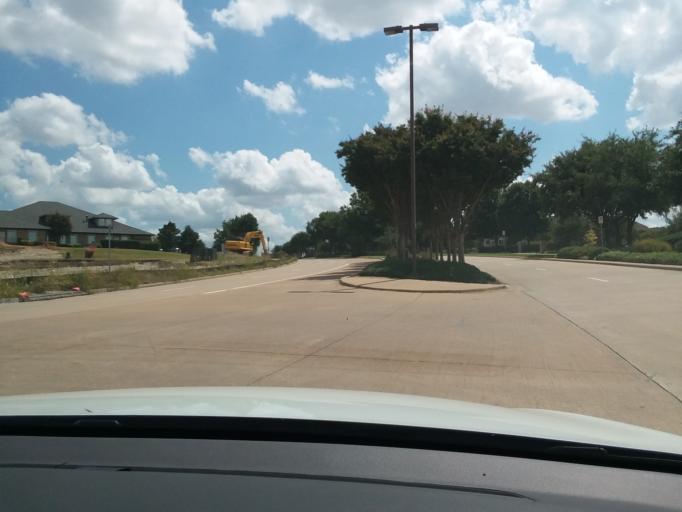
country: US
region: Texas
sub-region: Collin County
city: Prosper
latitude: 33.2170
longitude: -96.7216
